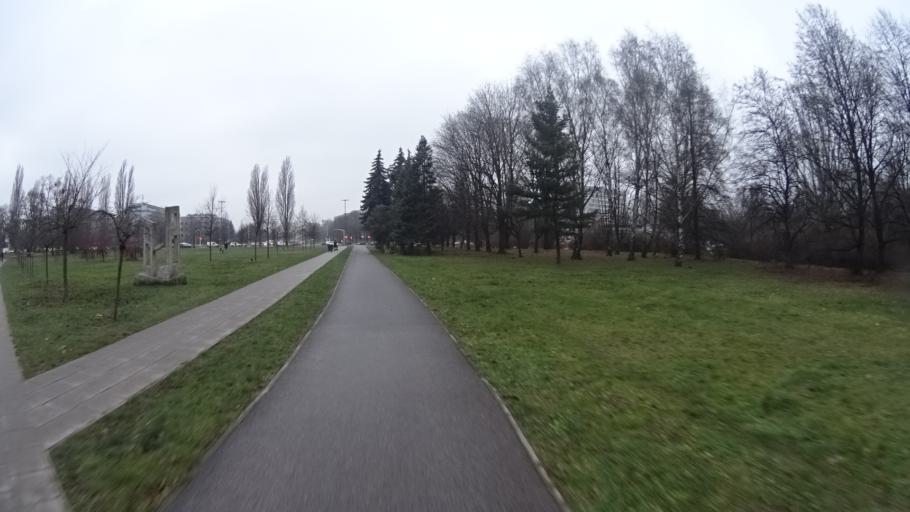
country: PL
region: Masovian Voivodeship
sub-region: Warszawa
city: Ochota
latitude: 52.2102
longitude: 20.9905
